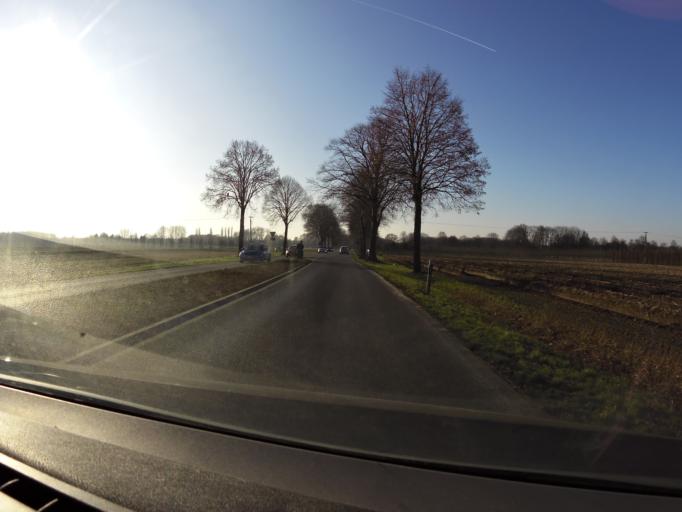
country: DE
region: North Rhine-Westphalia
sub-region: Regierungsbezirk Dusseldorf
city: Bruggen
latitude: 51.3066
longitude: 6.2108
